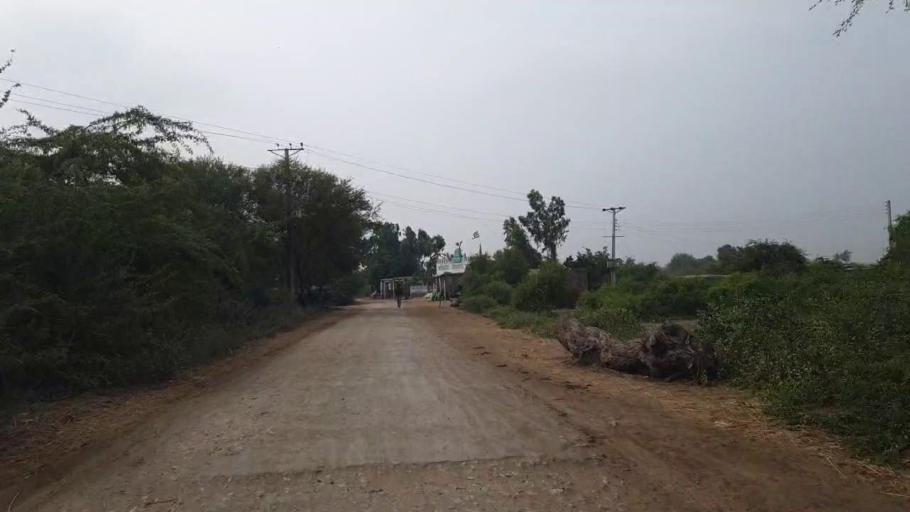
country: PK
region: Sindh
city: Matli
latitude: 24.9493
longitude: 68.5796
